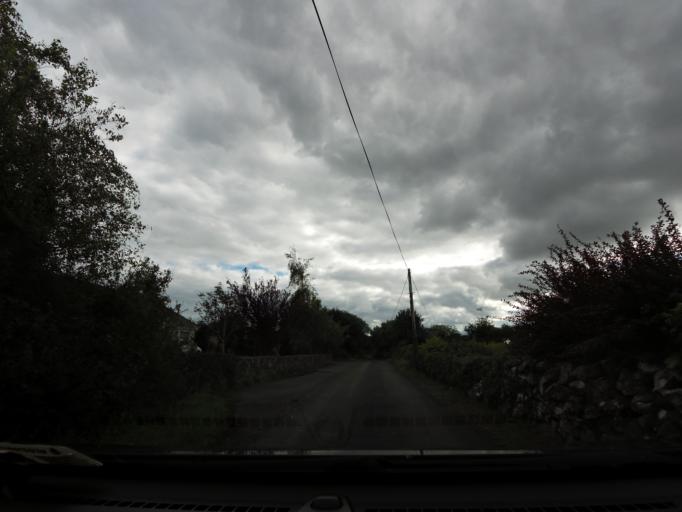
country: IE
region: Connaught
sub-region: County Galway
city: Moycullen
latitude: 53.3374
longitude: -9.1391
